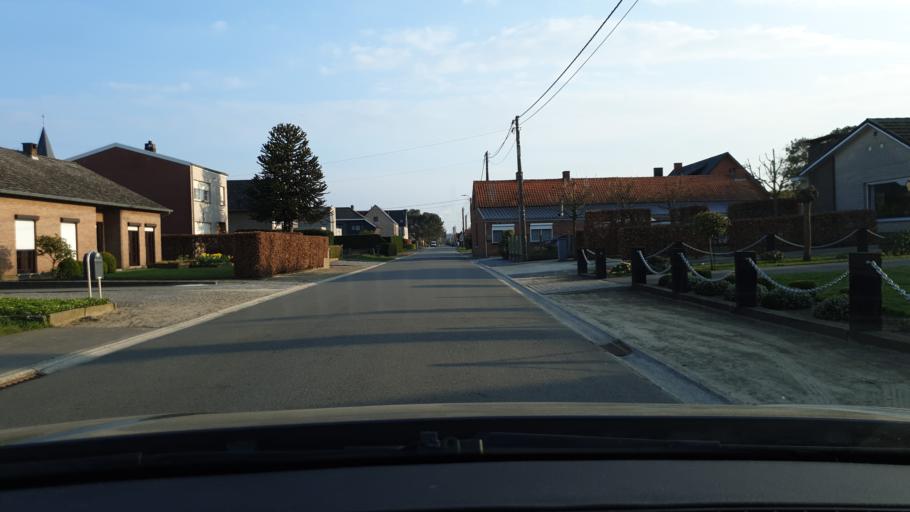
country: BE
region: Flanders
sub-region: Provincie Antwerpen
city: Geel
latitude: 51.1294
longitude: 5.0076
